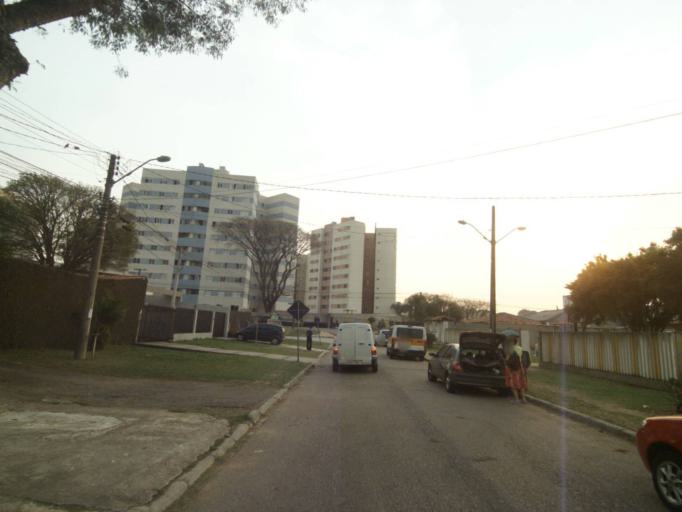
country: BR
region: Parana
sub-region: Curitiba
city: Curitiba
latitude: -25.4766
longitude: -49.2864
